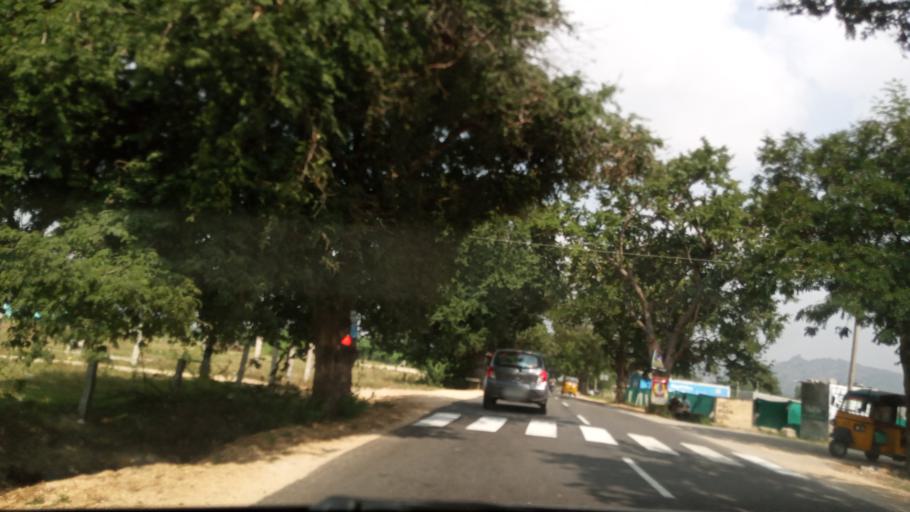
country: IN
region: Andhra Pradesh
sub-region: Chittoor
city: Madanapalle
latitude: 13.6272
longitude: 78.5500
